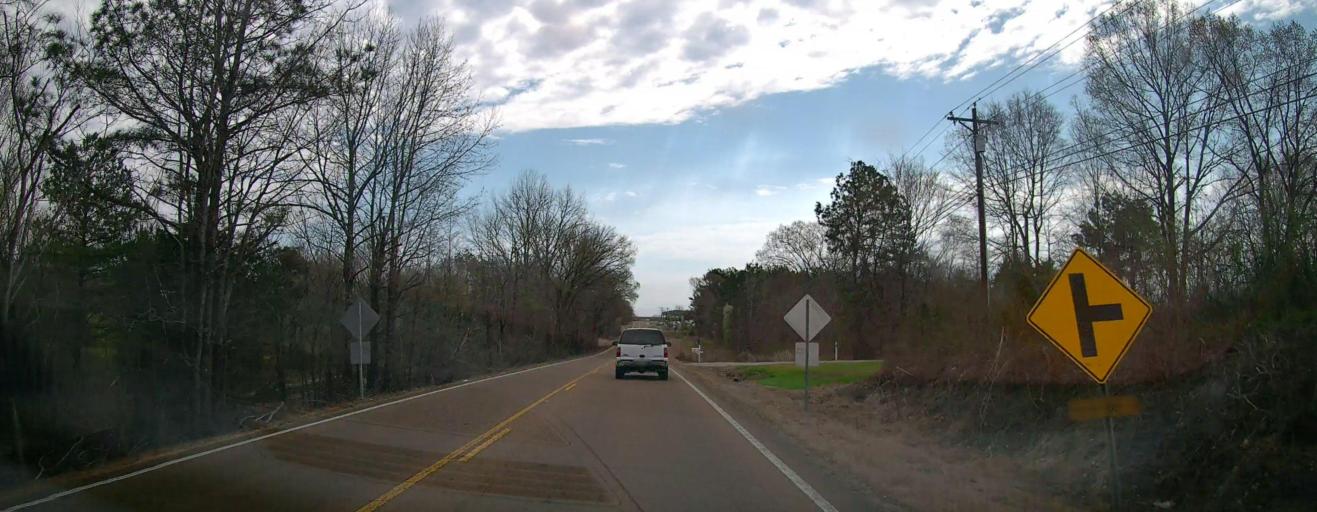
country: US
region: Mississippi
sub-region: Marshall County
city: Byhalia
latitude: 34.8878
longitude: -89.7276
